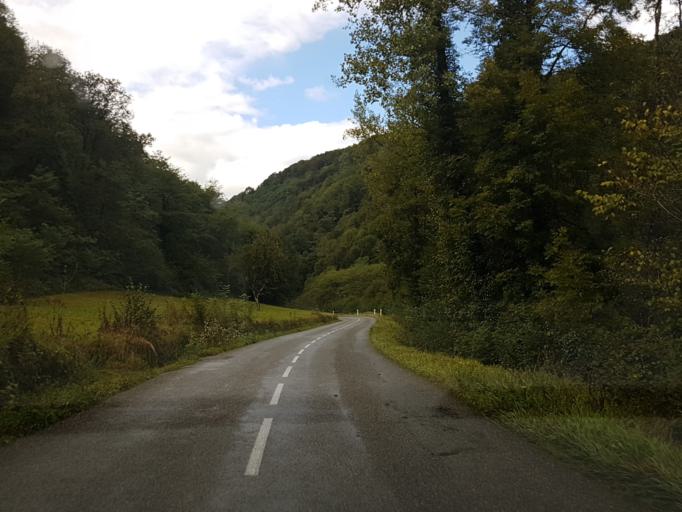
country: FR
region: Midi-Pyrenees
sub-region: Departement de l'Ariege
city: Saint-Girons
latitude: 42.9060
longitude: 1.2192
